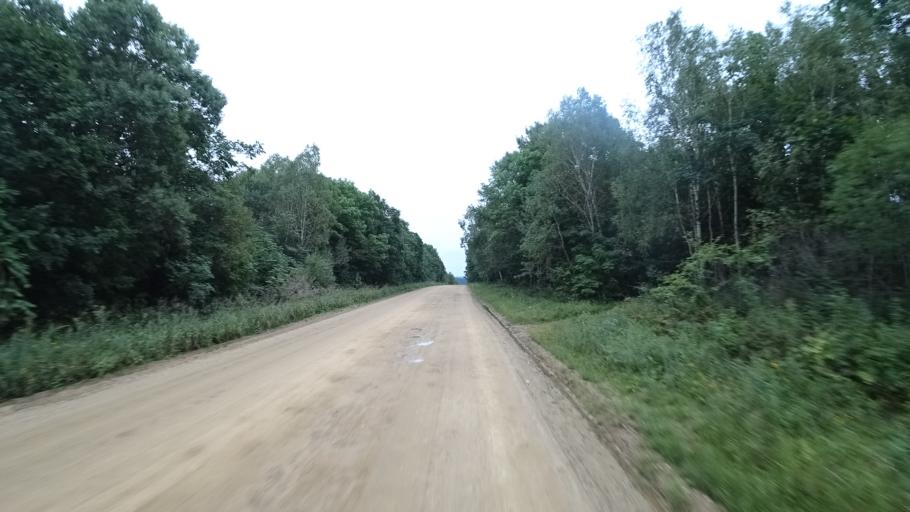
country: RU
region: Primorskiy
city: Rettikhovka
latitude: 44.1824
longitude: 132.8213
